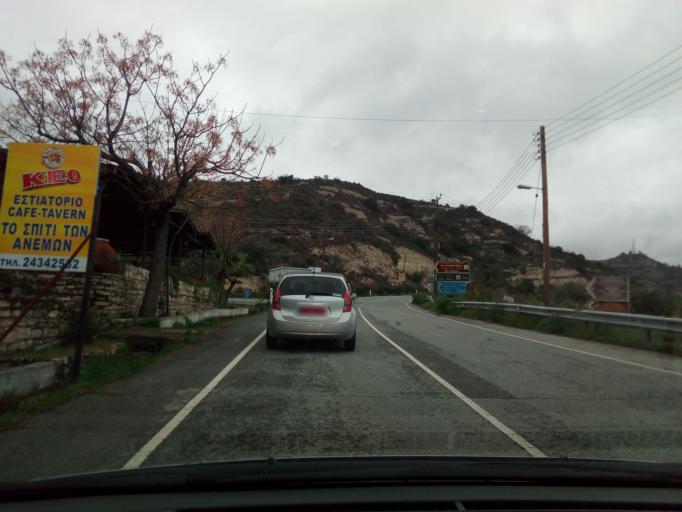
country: CY
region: Larnaka
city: Kofinou
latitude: 34.8572
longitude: 33.3127
